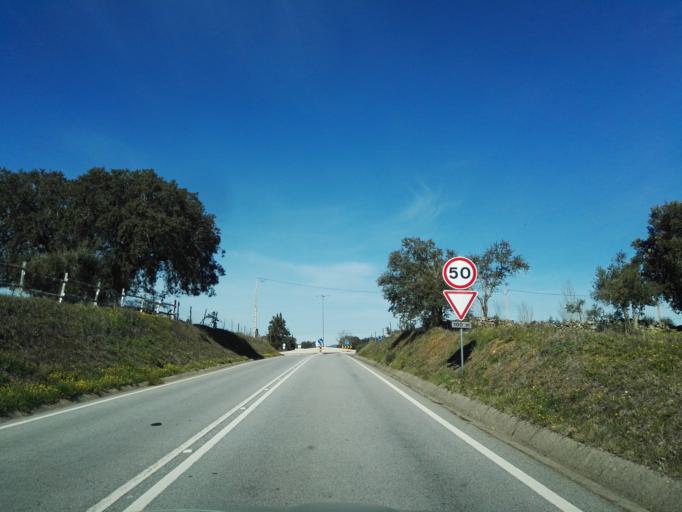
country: PT
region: Portalegre
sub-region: Arronches
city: Arronches
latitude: 39.1227
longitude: -7.2954
